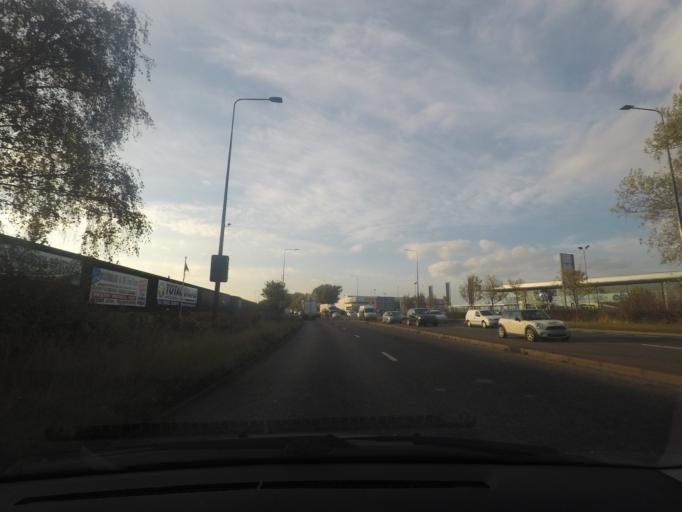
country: GB
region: England
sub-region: North East Lincolnshire
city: Grimbsy
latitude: 53.5759
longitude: -0.0985
